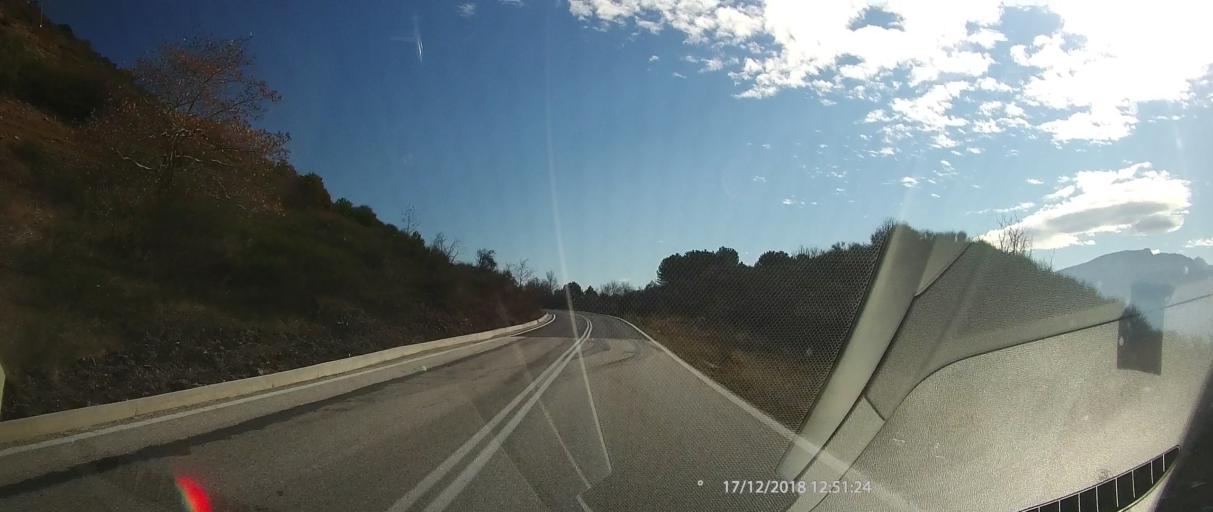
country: GR
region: Thessaly
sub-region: Trikala
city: Kastraki
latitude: 39.7668
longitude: 21.4643
